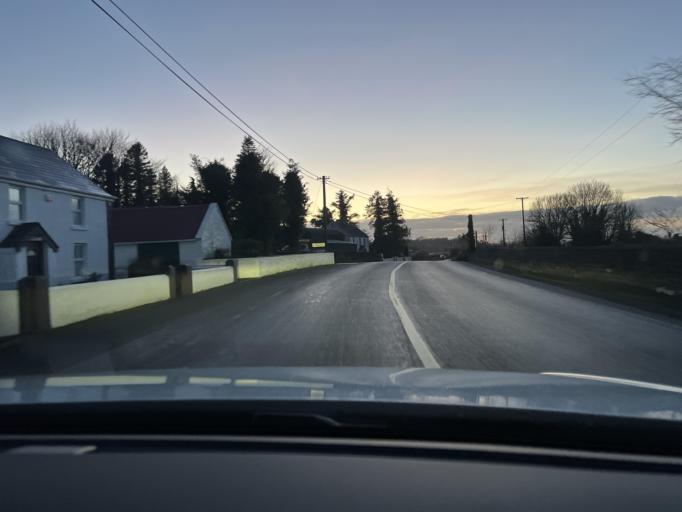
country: IE
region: Connaught
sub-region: County Leitrim
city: Carrick-on-Shannon
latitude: 53.9821
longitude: -8.0480
